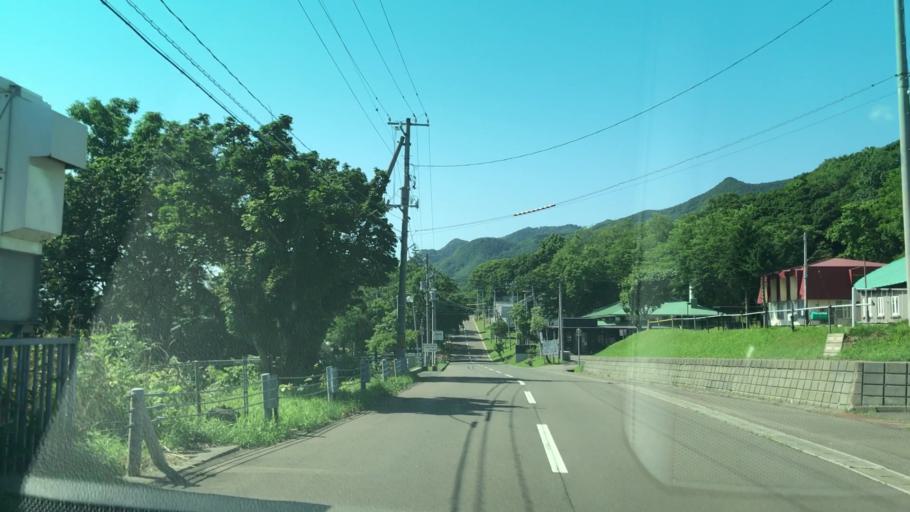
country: JP
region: Hokkaido
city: Iwanai
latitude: 43.1475
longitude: 140.4213
